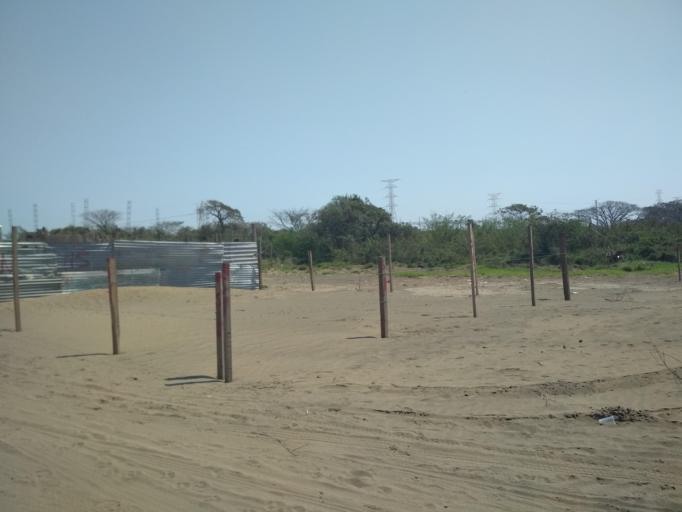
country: MX
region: Veracruz
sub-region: Veracruz
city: Lomas de Rio Medio Cuatro
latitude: 19.1871
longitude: -96.1968
